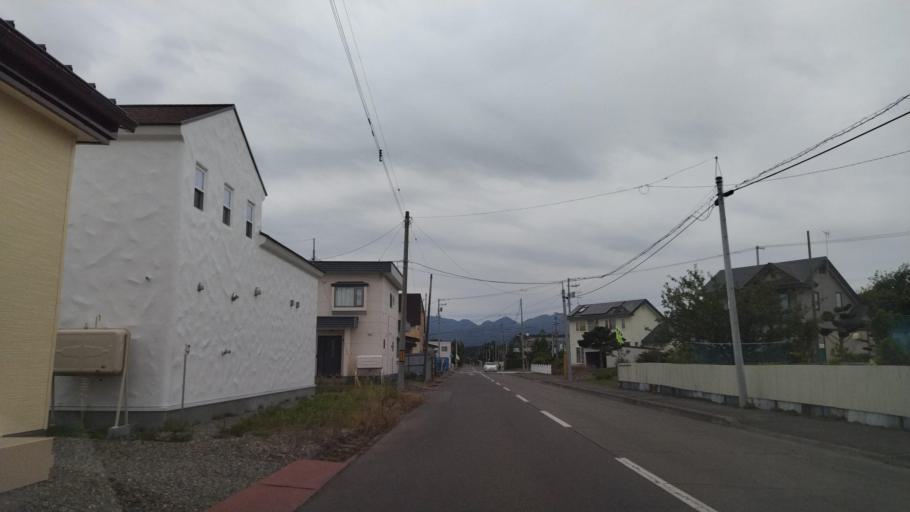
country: JP
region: Hokkaido
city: Otofuke
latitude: 43.2310
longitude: 143.2854
